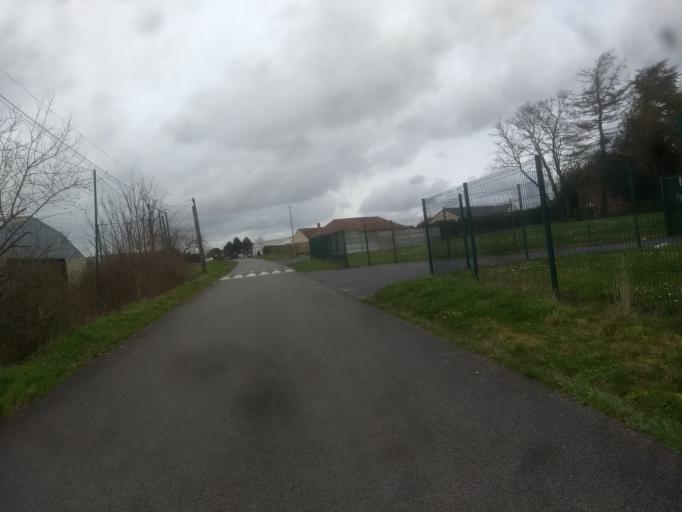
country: FR
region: Nord-Pas-de-Calais
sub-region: Departement du Pas-de-Calais
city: Sainte-Catherine
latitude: 50.3131
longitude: 2.7581
